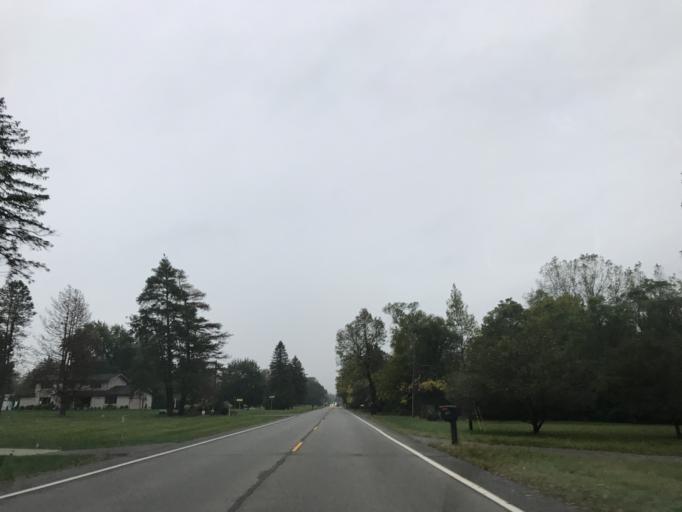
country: US
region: Michigan
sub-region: Oakland County
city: Farmington
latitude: 42.4638
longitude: -83.3179
